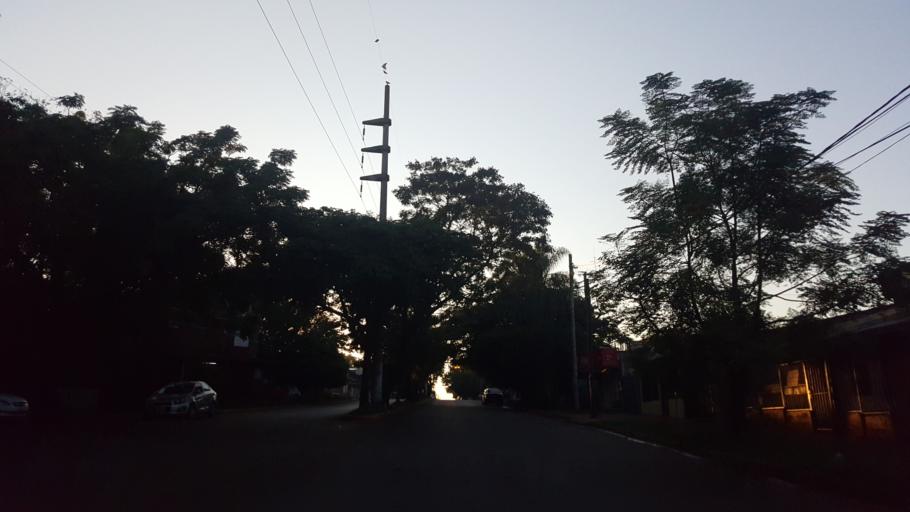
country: AR
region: Misiones
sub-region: Departamento de Capital
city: Posadas
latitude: -27.3721
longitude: -55.9489
